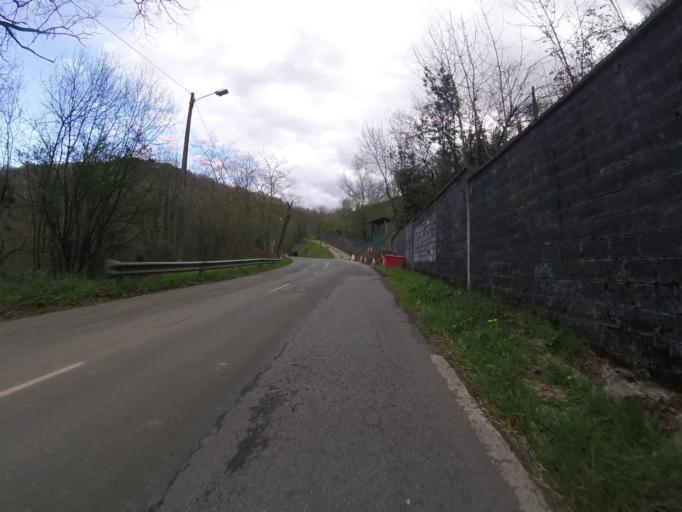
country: ES
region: Basque Country
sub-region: Provincia de Guipuzcoa
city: Errenteria
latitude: 43.2881
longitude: -1.8561
